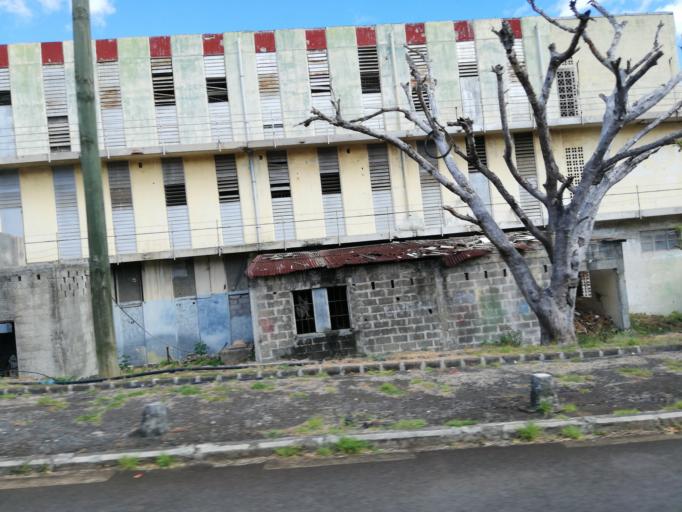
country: MU
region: Moka
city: Pailles
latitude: -20.1897
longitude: 57.4672
